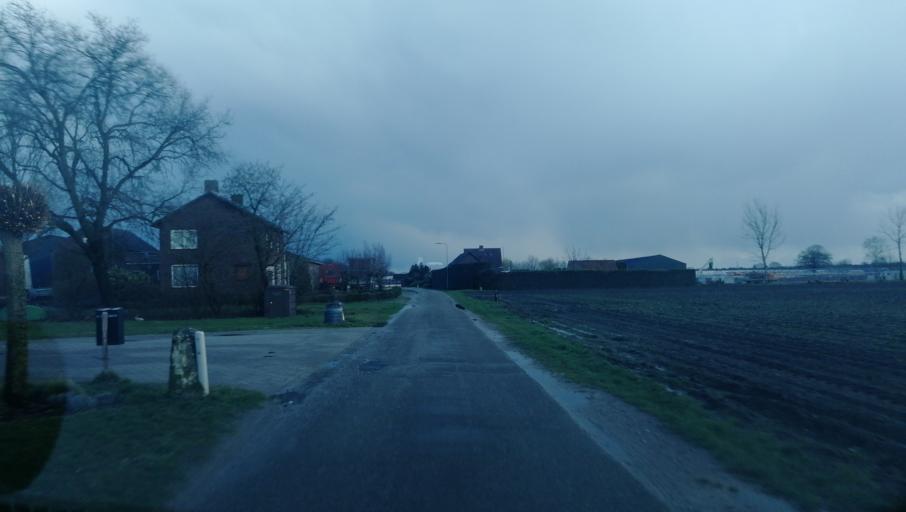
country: NL
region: Limburg
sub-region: Gemeente Peel en Maas
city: Maasbree
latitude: 51.3480
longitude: 6.0470
